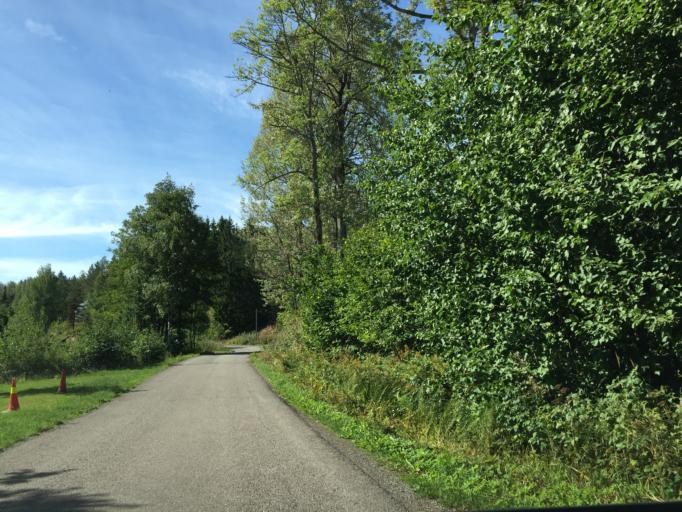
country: NO
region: Vestfold
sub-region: Hof
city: Hof
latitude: 59.4751
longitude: 10.1446
